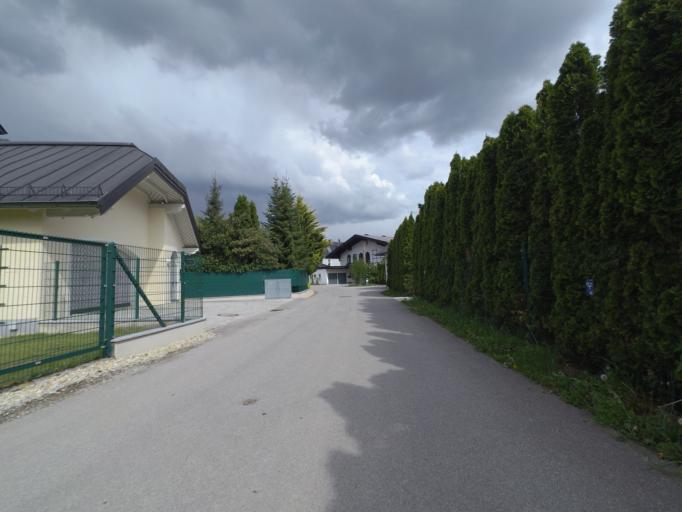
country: AT
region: Salzburg
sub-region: Politischer Bezirk Salzburg-Umgebung
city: Anif
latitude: 47.7498
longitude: 13.0600
